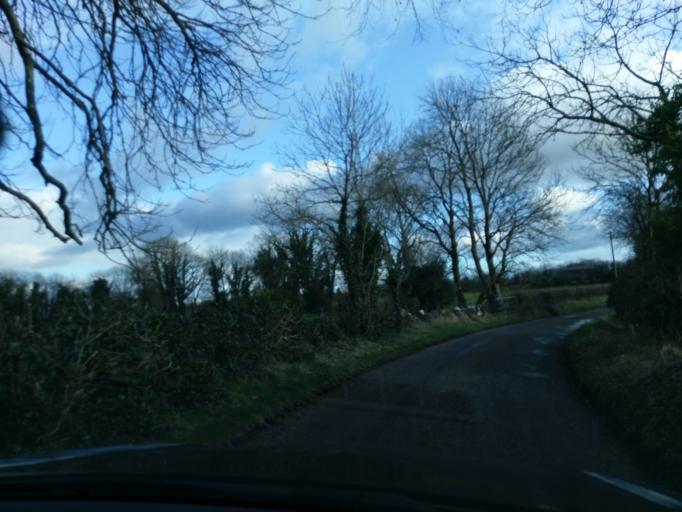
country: IE
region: Connaught
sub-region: County Galway
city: Athenry
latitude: 53.3653
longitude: -8.6488
